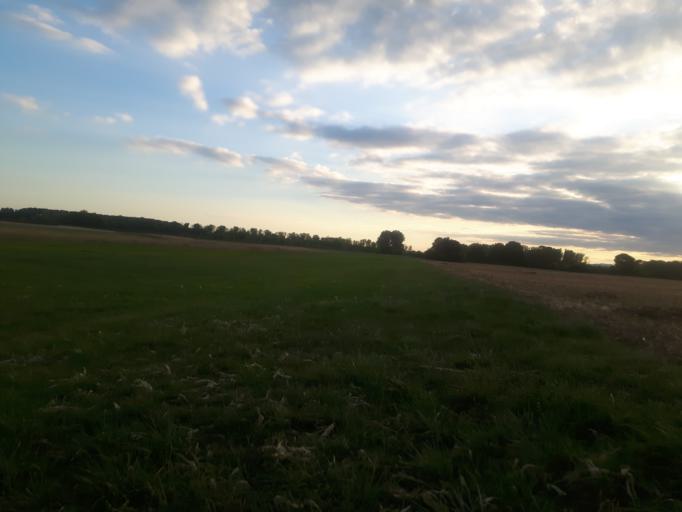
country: DE
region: Rheinland-Pfalz
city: Otterstadt
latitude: 49.3871
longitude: 8.4774
